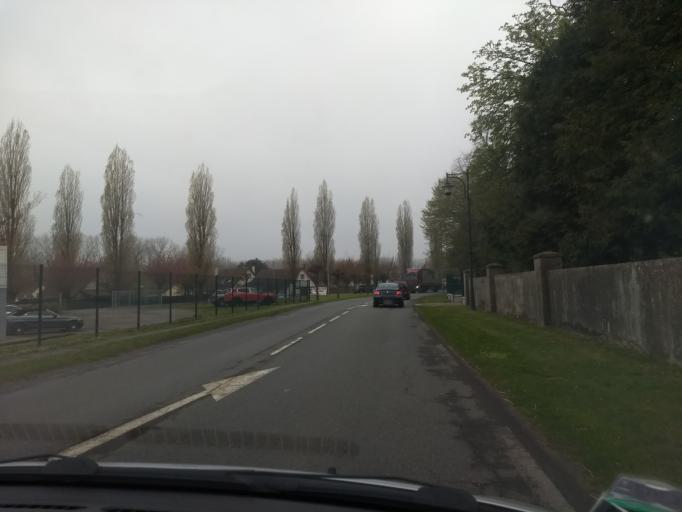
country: FR
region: Nord-Pas-de-Calais
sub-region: Departement du Pas-de-Calais
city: Verton
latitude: 50.4053
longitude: 1.6485
